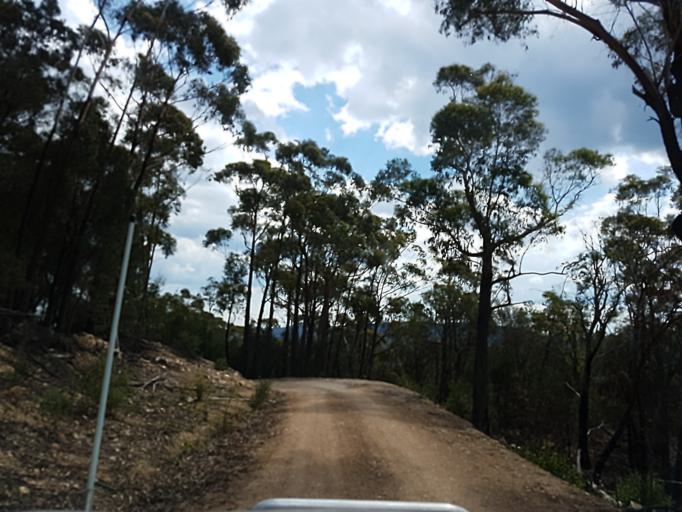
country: AU
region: Victoria
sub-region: East Gippsland
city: Lakes Entrance
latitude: -37.4053
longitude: 148.2332
